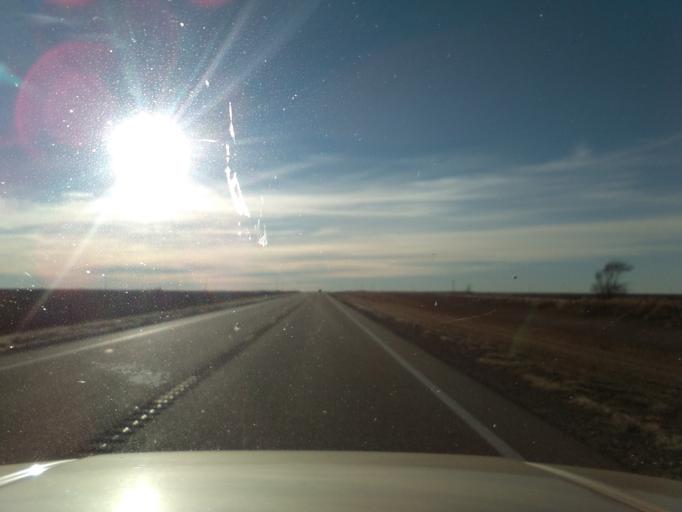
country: US
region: Kansas
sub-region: Sheridan County
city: Hoxie
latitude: 39.4980
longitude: -100.6743
